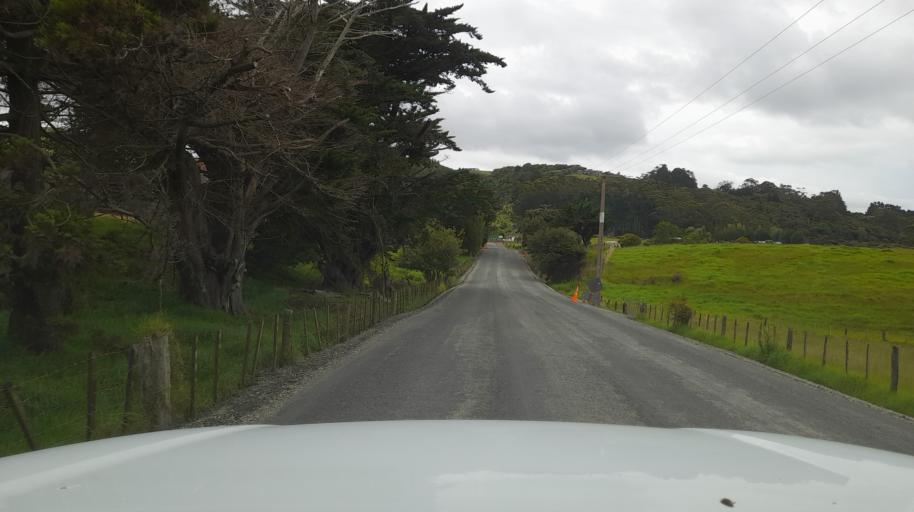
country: NZ
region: Northland
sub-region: Far North District
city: Ahipara
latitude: -35.1668
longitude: 173.1900
